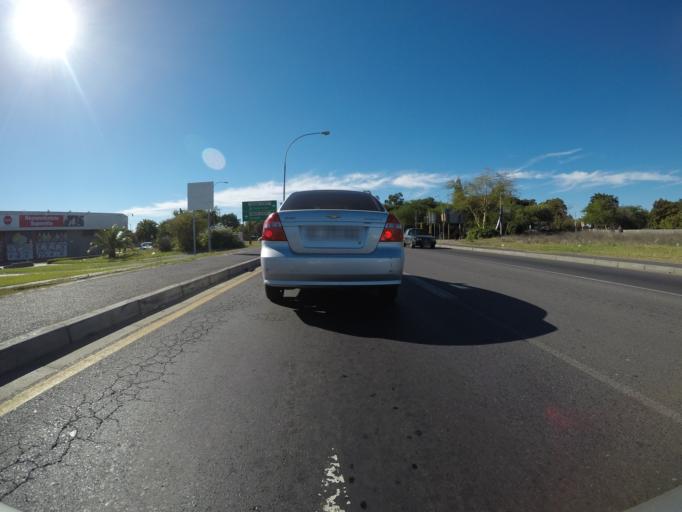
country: ZA
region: Western Cape
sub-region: City of Cape Town
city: Kraaifontein
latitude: -33.9350
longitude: 18.6765
